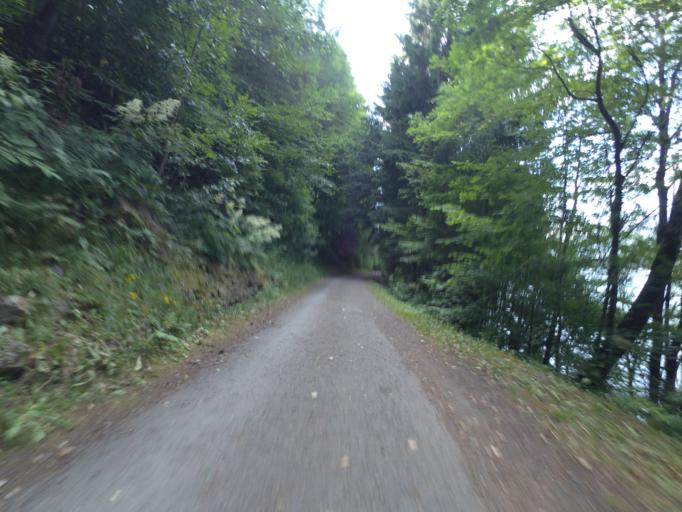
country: AT
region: Carinthia
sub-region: Politischer Bezirk Villach Land
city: Ferndorf
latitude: 46.7704
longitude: 13.6128
